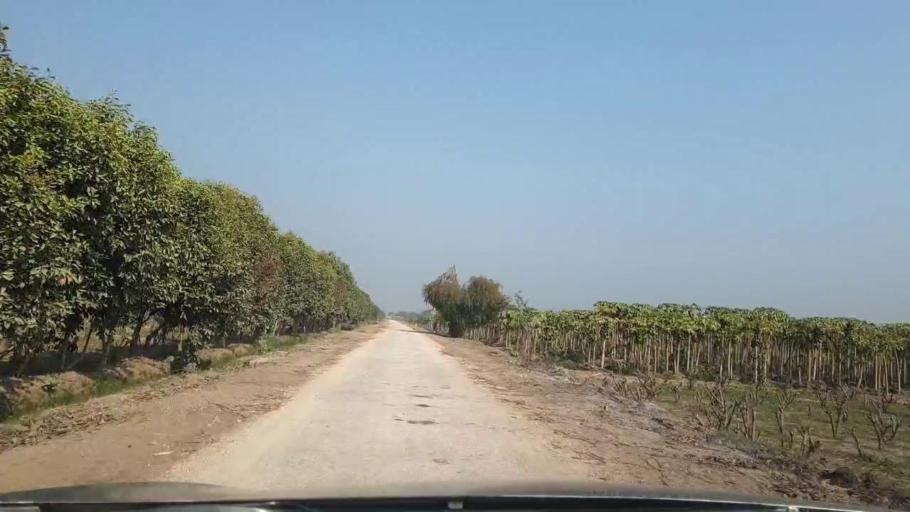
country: PK
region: Sindh
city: Tando Allahyar
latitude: 25.5140
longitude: 68.7631
